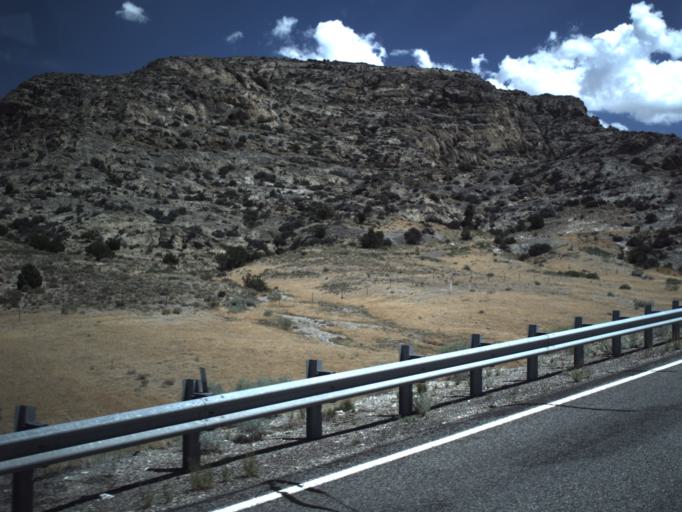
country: US
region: Utah
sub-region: Beaver County
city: Milford
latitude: 39.0719
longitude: -113.6595
